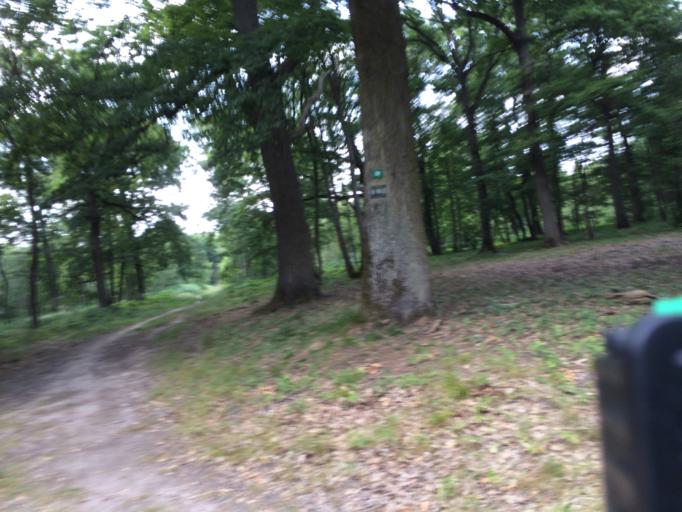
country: FR
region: Ile-de-France
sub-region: Departement de l'Essonne
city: Soisy-sur-Seine
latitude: 48.6645
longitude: 2.4499
